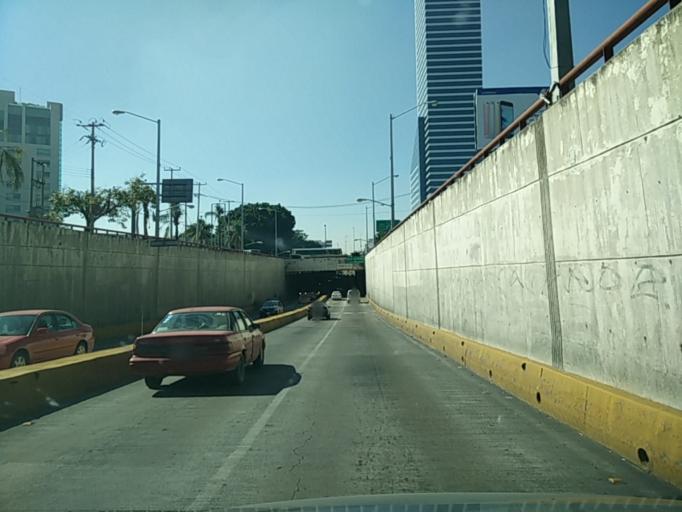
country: MX
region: Jalisco
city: Guadalajara
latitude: 20.6680
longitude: -103.3917
